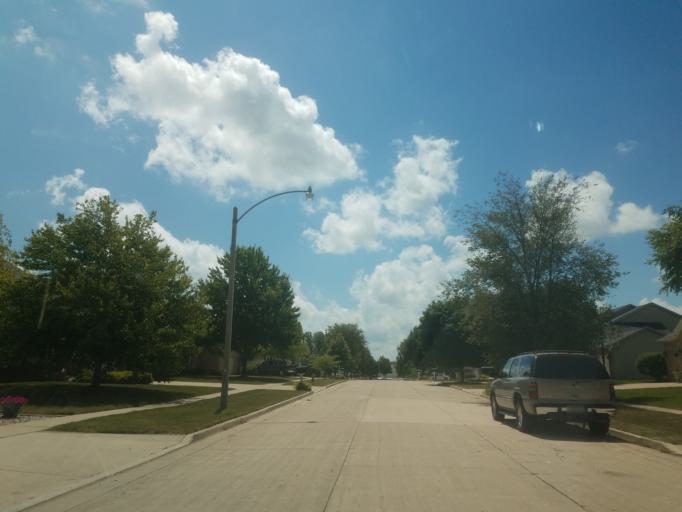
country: US
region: Illinois
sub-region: McLean County
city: Normal
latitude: 40.4975
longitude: -88.9139
